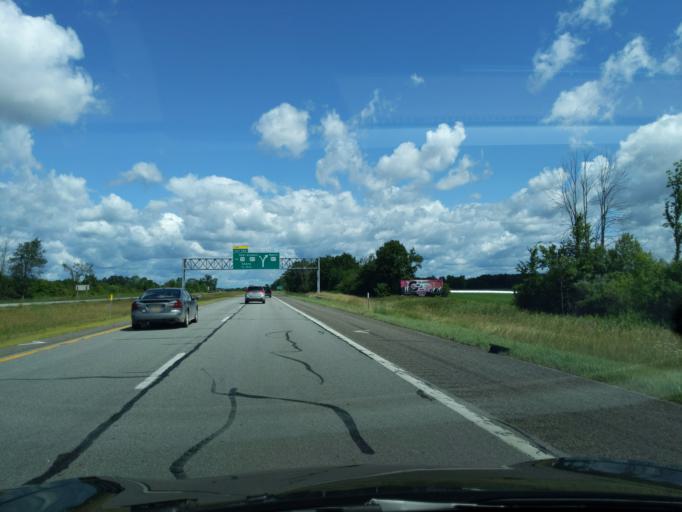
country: US
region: Michigan
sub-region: Clare County
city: Clare
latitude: 43.7879
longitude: -84.7584
